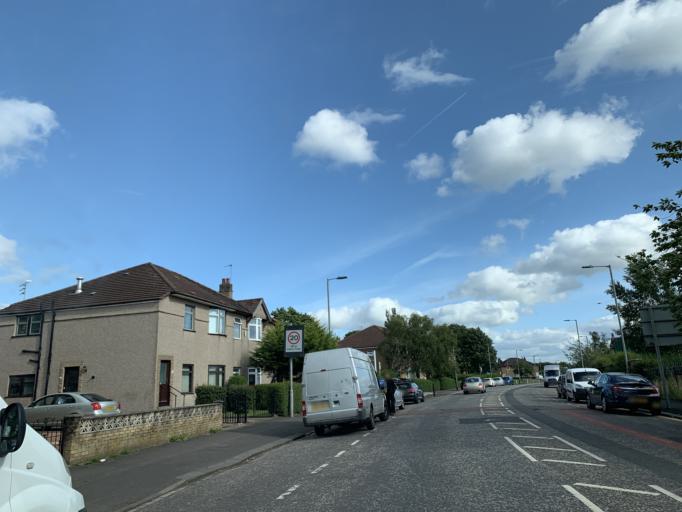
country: GB
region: Scotland
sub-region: Renfrewshire
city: Renfrew
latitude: 55.8508
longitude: -4.3614
